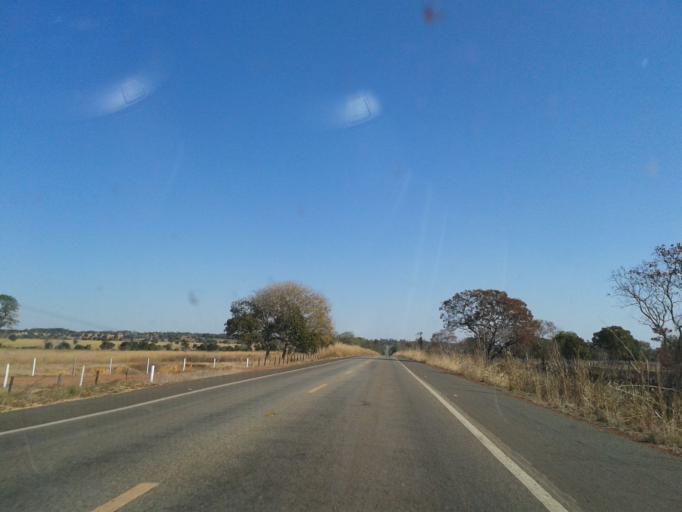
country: BR
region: Goias
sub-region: Mozarlandia
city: Mozarlandia
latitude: -15.0574
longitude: -50.6124
